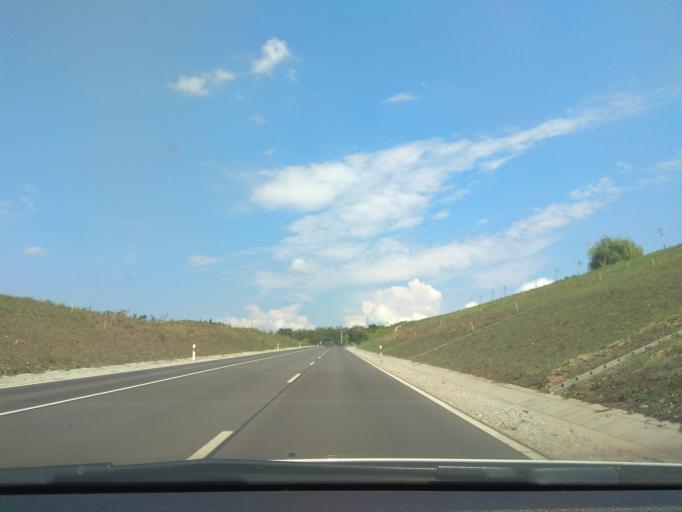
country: HU
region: Heves
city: Andornaktalya
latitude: 47.8329
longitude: 20.4222
